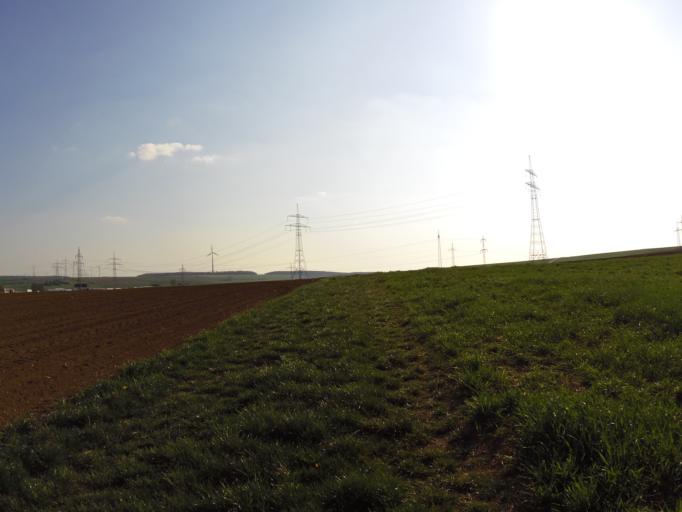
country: DE
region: Bavaria
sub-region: Regierungsbezirk Unterfranken
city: Biebelried
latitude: 49.7658
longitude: 10.0573
